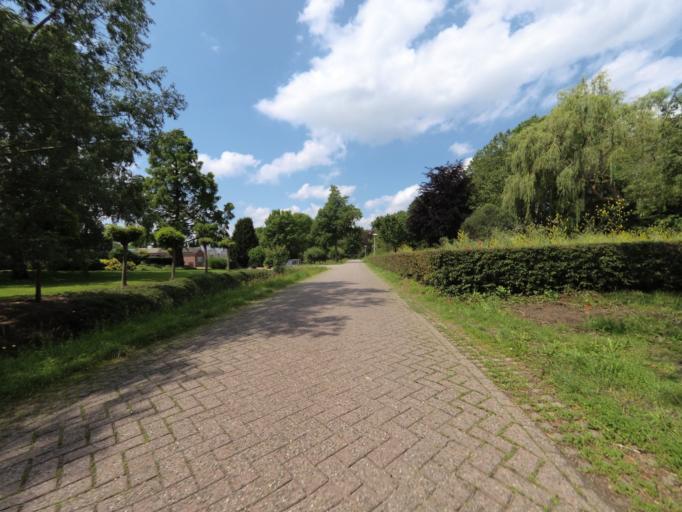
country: NL
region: Utrecht
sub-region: Gemeente Wijk bij Duurstede
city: Wijk bij Duurstede
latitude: 51.9700
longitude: 5.3388
